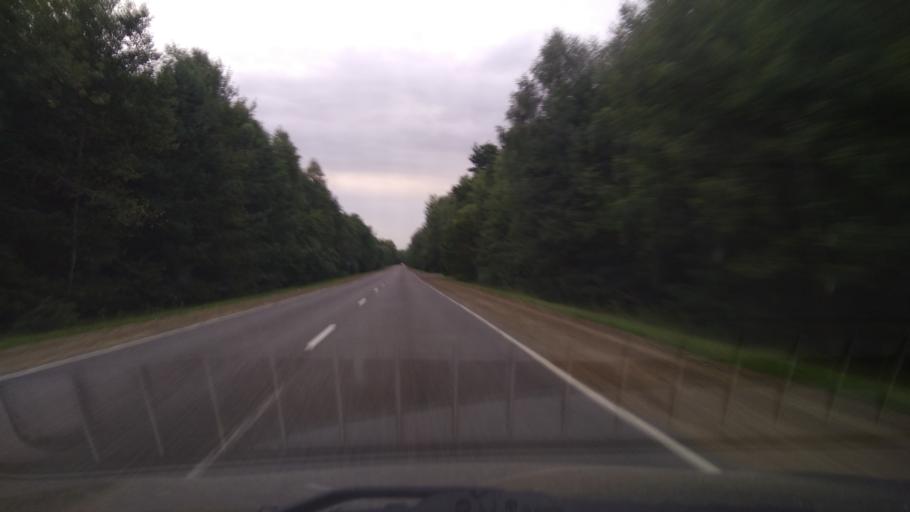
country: BY
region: Brest
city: Byaroza
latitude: 52.4078
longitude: 24.9969
